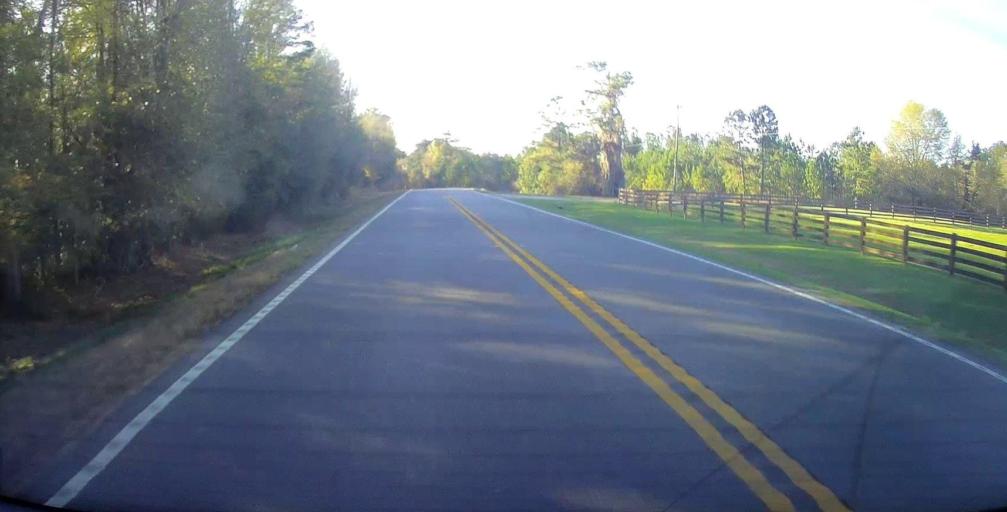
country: US
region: Georgia
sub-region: Pulaski County
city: Hawkinsville
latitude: 32.2684
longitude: -83.4335
